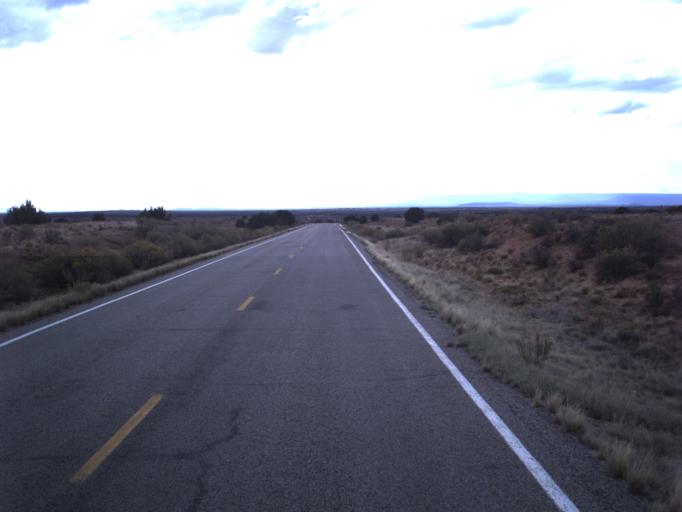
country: US
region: Utah
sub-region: San Juan County
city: Blanding
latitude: 37.4349
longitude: -109.3780
